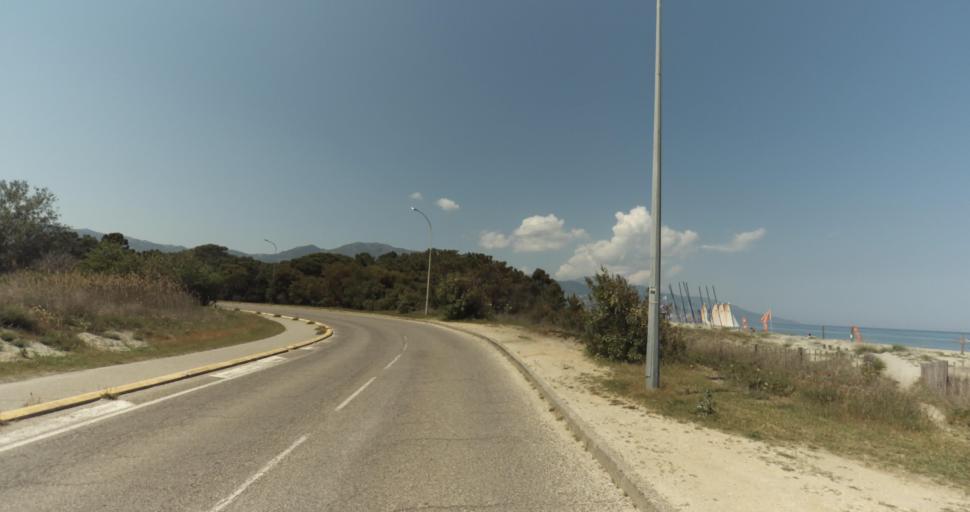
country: FR
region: Corsica
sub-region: Departement de la Haute-Corse
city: Biguglia
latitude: 42.6425
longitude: 9.4597
